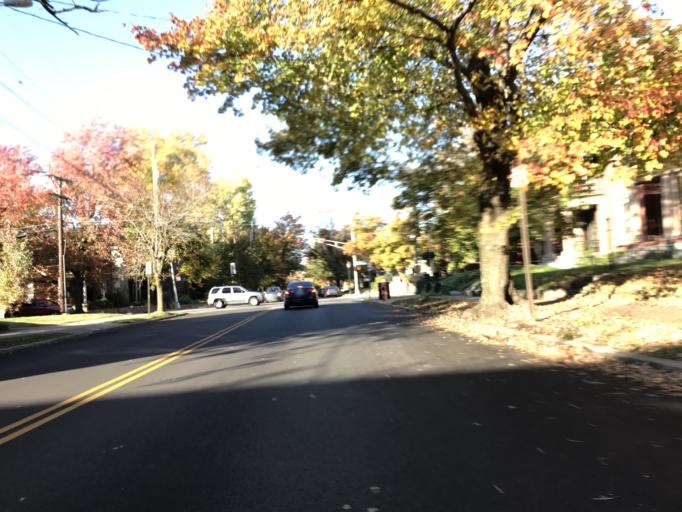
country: US
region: Kentucky
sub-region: Jefferson County
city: Louisville
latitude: 38.2229
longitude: -85.7624
